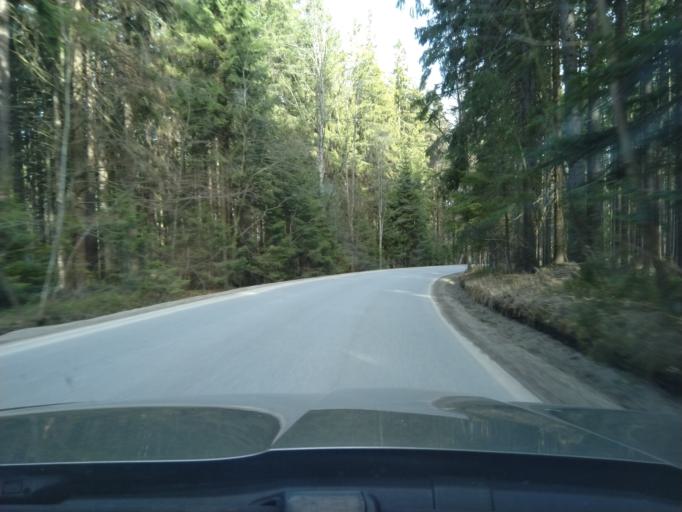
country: CZ
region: Jihocesky
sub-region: Okres Prachatice
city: Stachy
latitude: 49.0667
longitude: 13.6499
